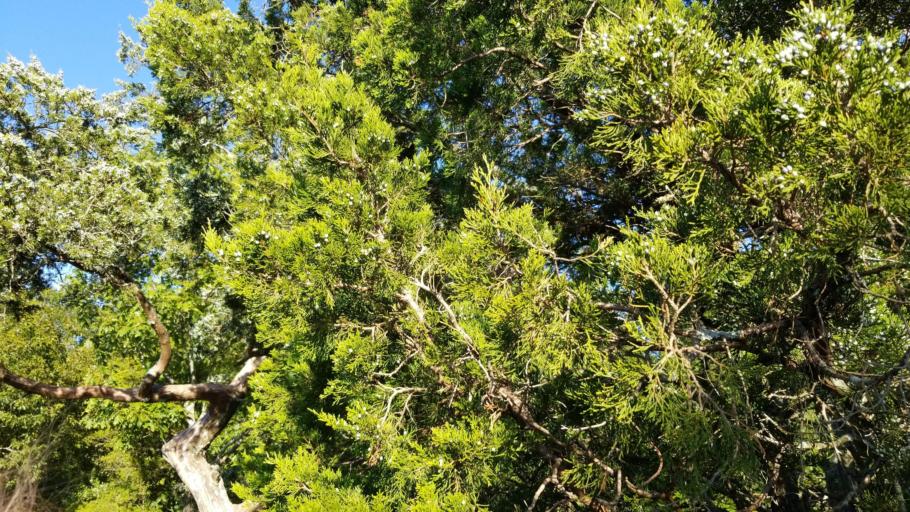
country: US
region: Illinois
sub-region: Hardin County
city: Elizabethtown
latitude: 37.6028
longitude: -88.3858
